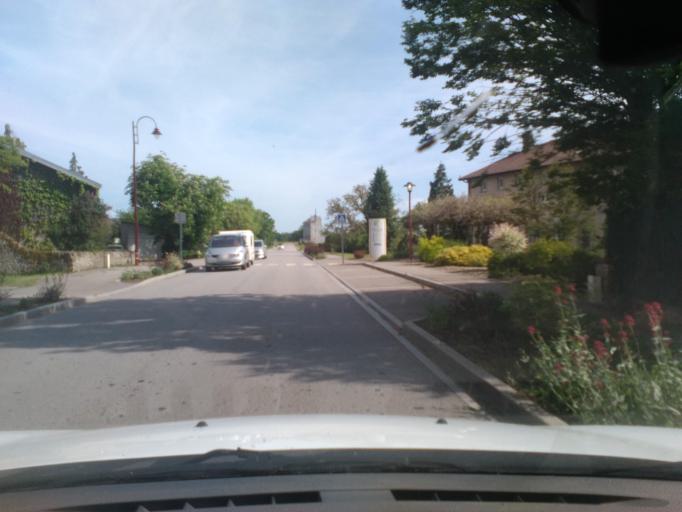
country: FR
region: Lorraine
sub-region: Departement des Vosges
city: Rambervillers
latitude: 48.3833
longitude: 6.6044
